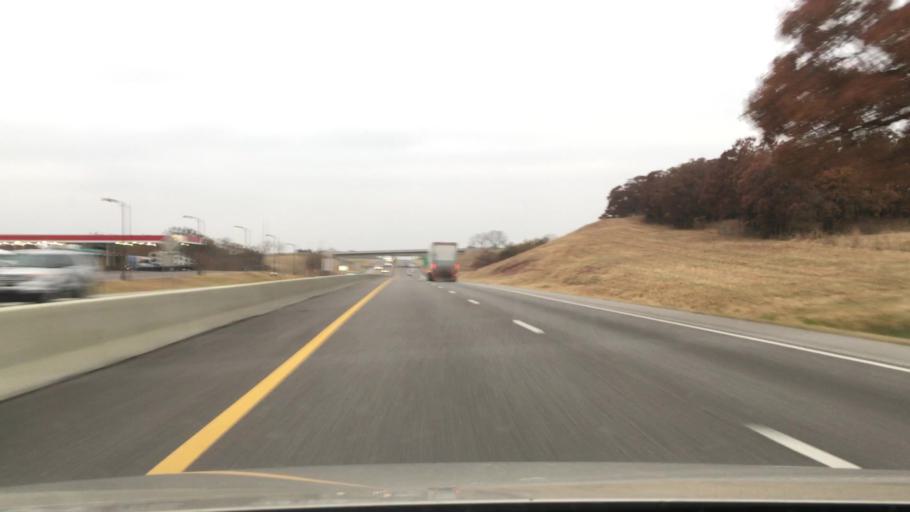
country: US
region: Oklahoma
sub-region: Lincoln County
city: Chandler
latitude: 35.7201
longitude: -96.8790
